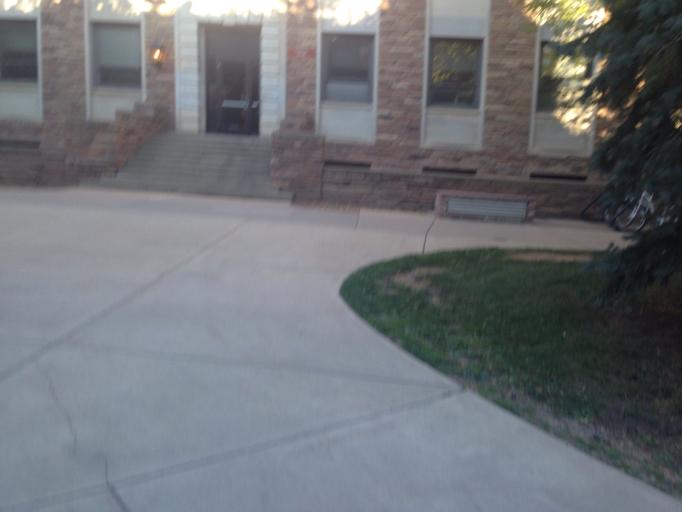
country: US
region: Colorado
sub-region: Boulder County
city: Boulder
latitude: 40.0086
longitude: -105.2699
